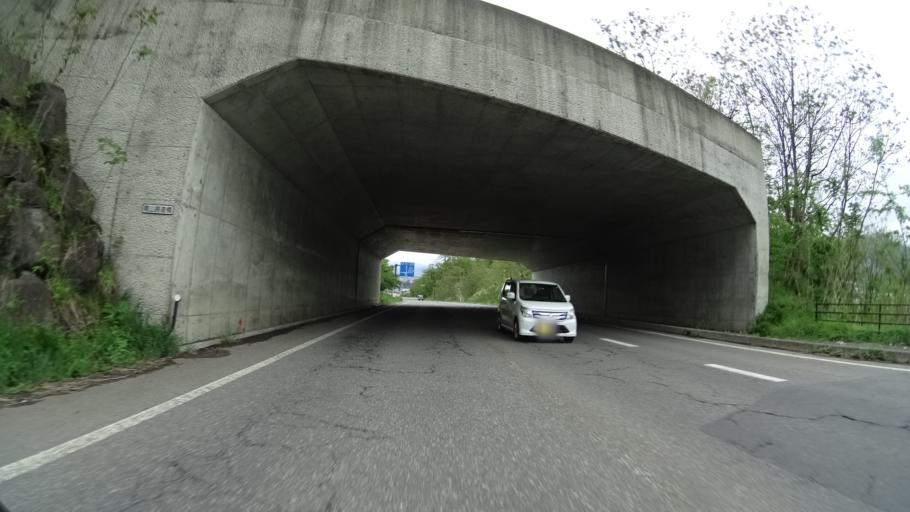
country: JP
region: Nagano
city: Nakano
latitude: 36.7536
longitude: 138.3961
